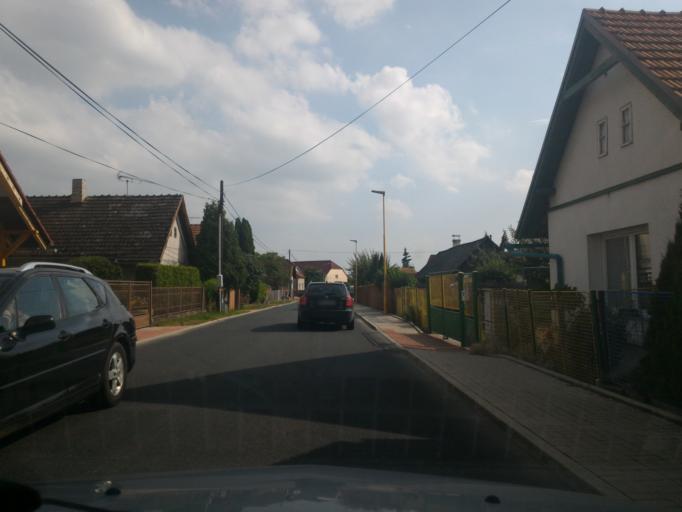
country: CZ
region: Central Bohemia
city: Loucen
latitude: 50.2408
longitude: 15.0223
